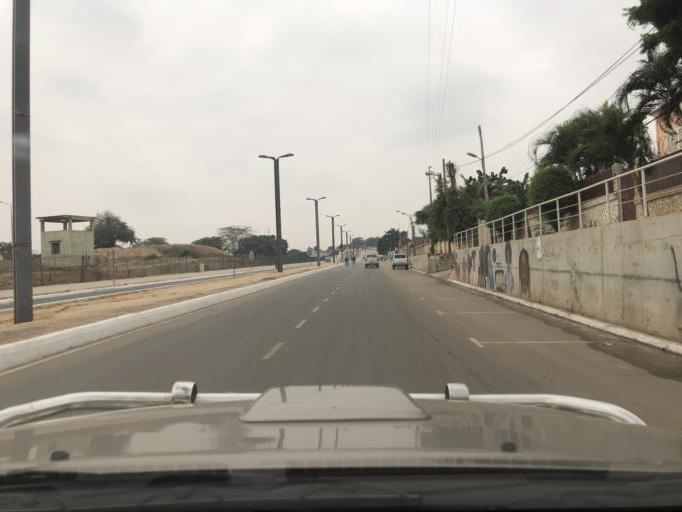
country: AO
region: Luanda
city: Luanda
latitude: -8.9081
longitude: 13.1675
